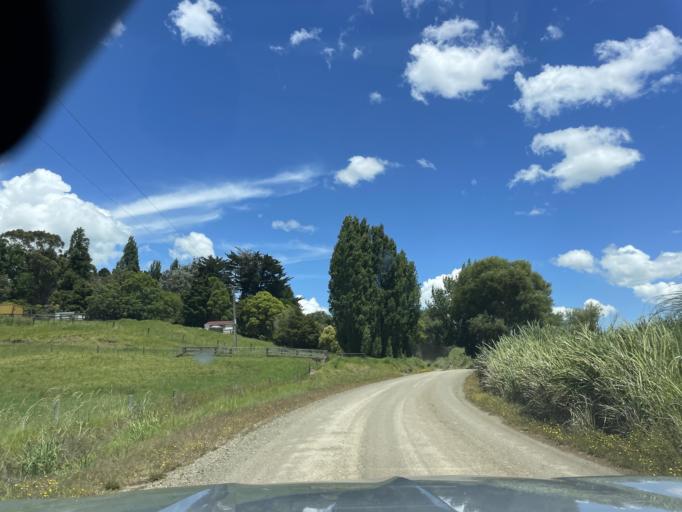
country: NZ
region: Northland
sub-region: Kaipara District
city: Dargaville
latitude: -35.9057
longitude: 173.9226
